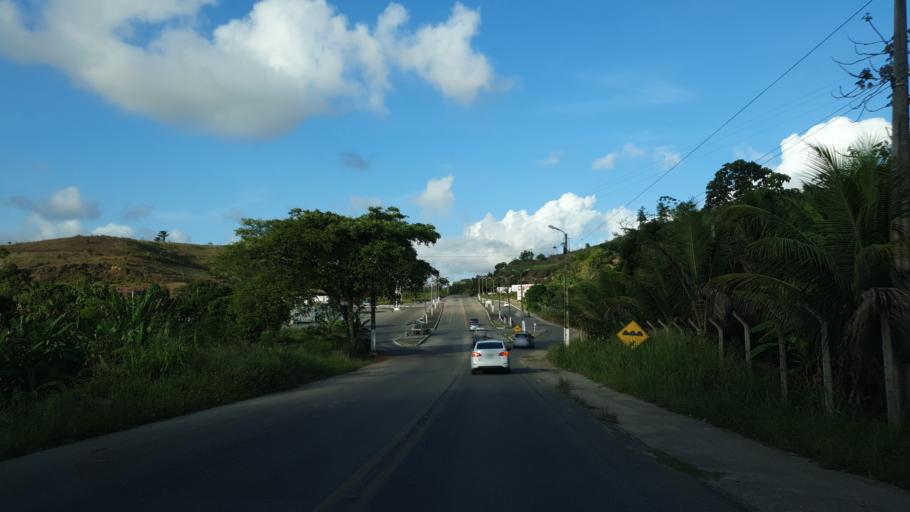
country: BR
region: Pernambuco
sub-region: Barreiros
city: Barreiros
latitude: -8.7921
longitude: -35.1864
